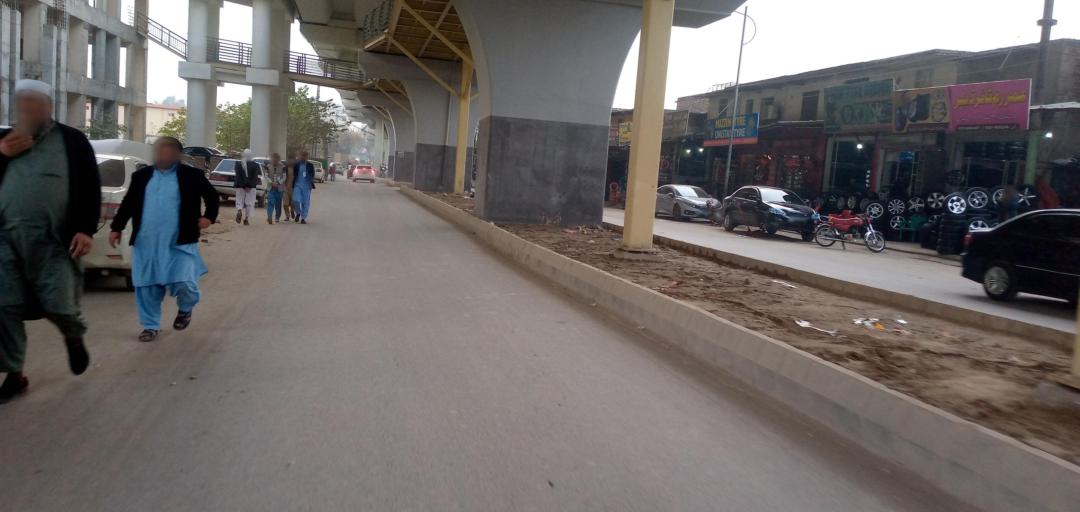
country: PK
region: Khyber Pakhtunkhwa
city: Peshawar
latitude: 34.0063
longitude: 71.5583
